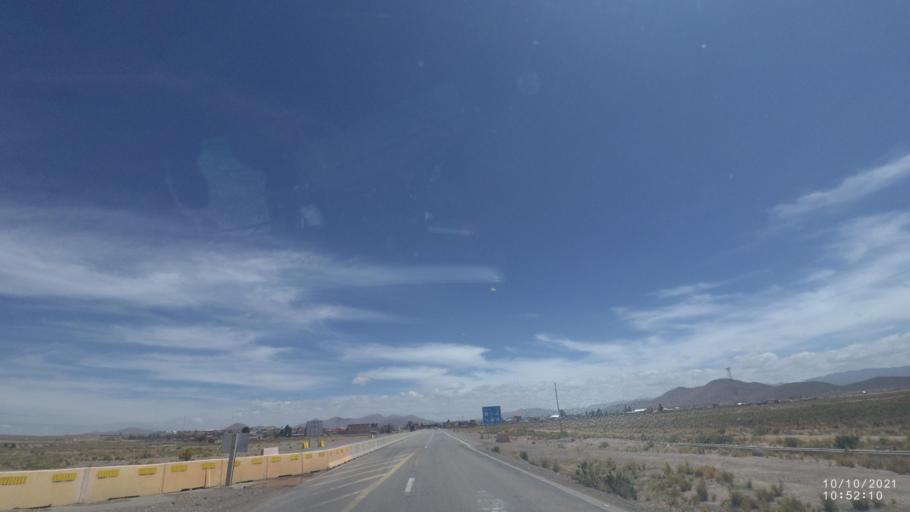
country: BO
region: La Paz
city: Colquiri
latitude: -17.6563
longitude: -67.2071
